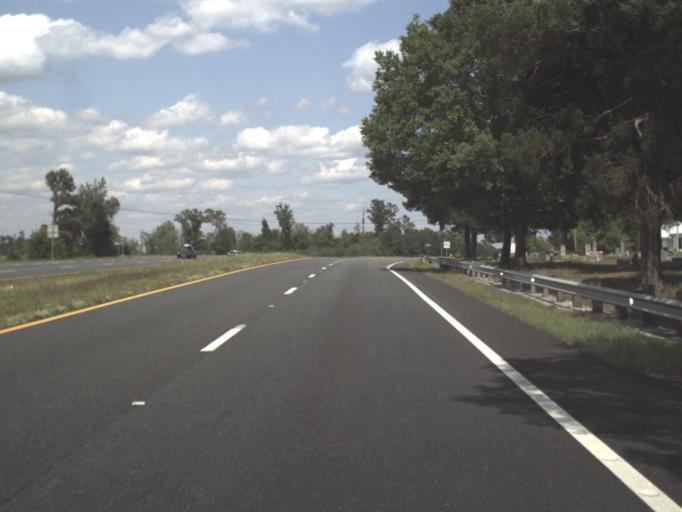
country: US
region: Florida
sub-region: Escambia County
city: Century
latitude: 30.9299
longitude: -87.3021
